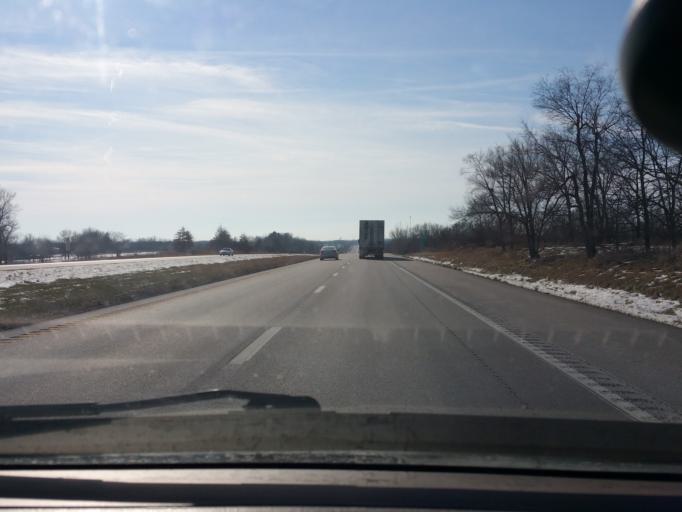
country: US
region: Missouri
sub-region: Clinton County
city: Cameron
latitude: 39.7820
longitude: -94.2087
